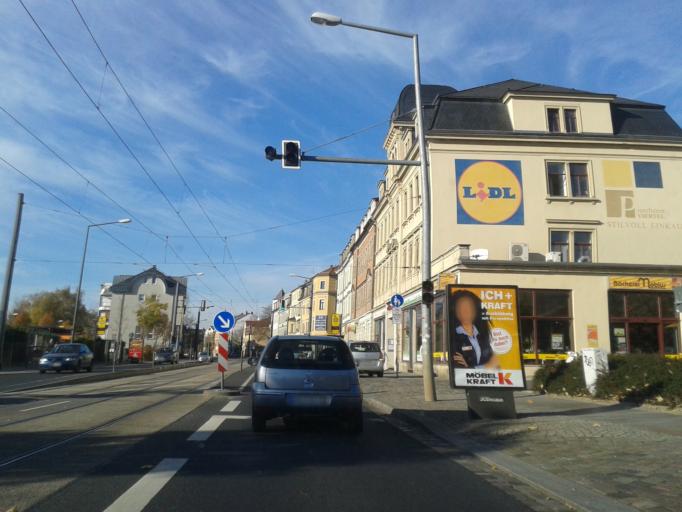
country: DE
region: Saxony
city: Dresden
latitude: 51.0741
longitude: 13.7239
